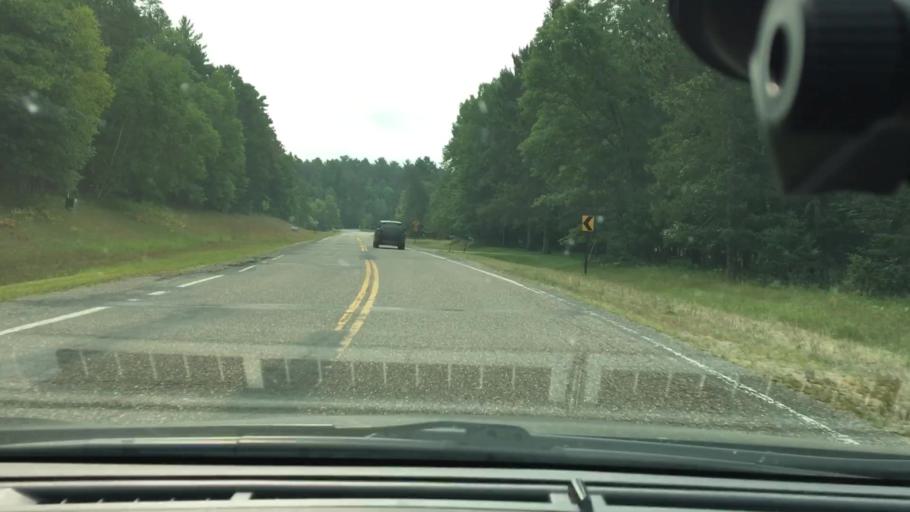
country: US
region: Minnesota
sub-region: Crow Wing County
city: Cross Lake
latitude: 46.6559
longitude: -94.1000
